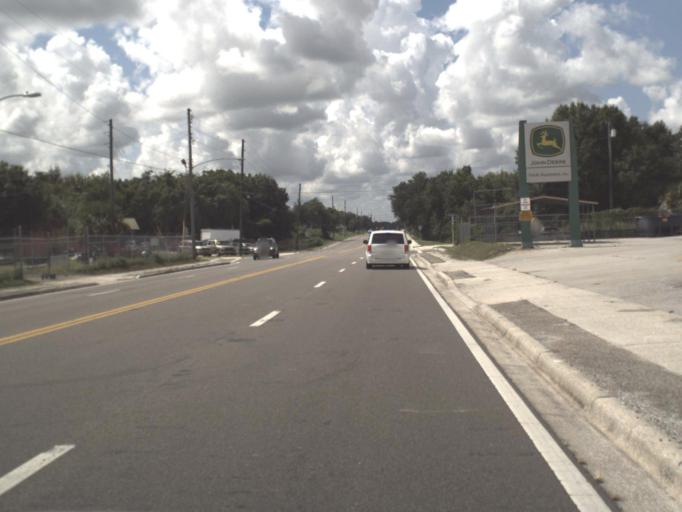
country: US
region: Florida
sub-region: Hardee County
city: Zolfo Springs
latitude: 27.4921
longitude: -81.7964
